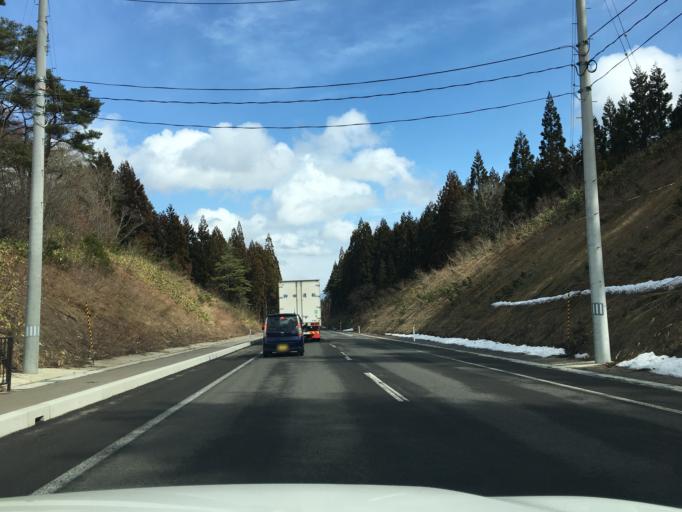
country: JP
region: Akita
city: Takanosu
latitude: 40.1076
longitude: 140.3542
